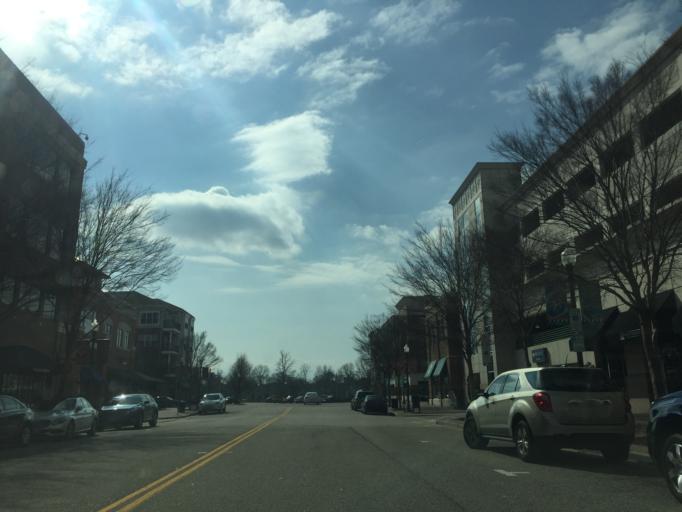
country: US
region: Virginia
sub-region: City of Newport News
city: Newport News
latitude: 37.0868
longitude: -76.4741
